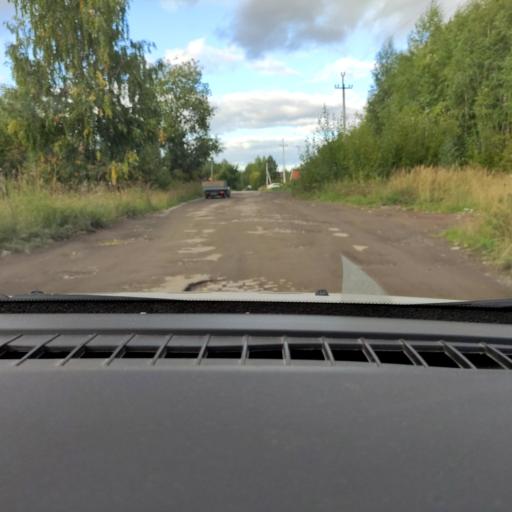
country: RU
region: Perm
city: Perm
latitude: 58.1120
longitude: 56.3878
